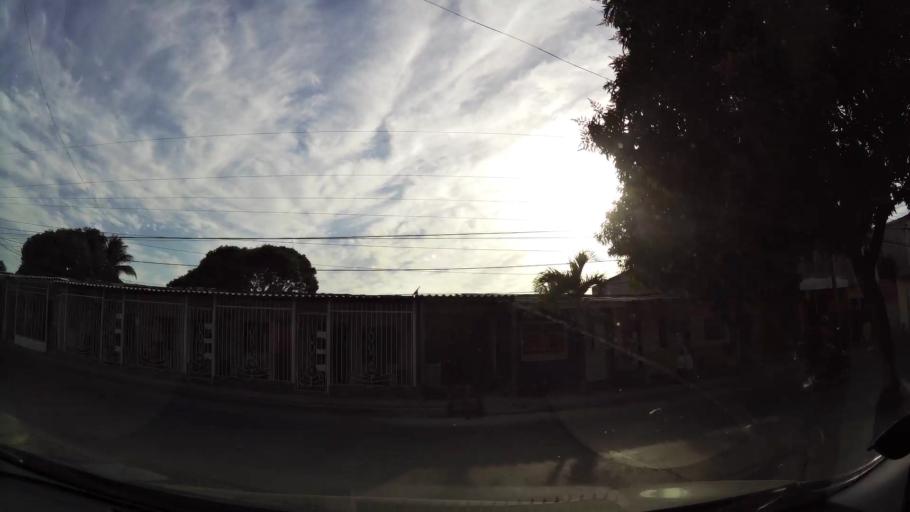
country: CO
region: Atlantico
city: Barranquilla
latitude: 10.9442
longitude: -74.8199
